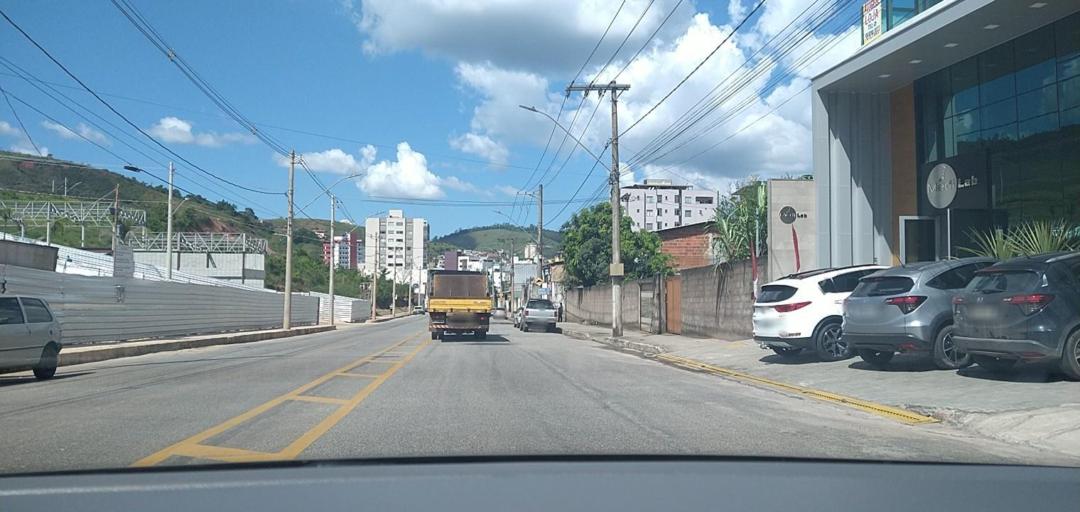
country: BR
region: Minas Gerais
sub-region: Joao Monlevade
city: Joao Monlevade
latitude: -19.8091
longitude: -43.1868
